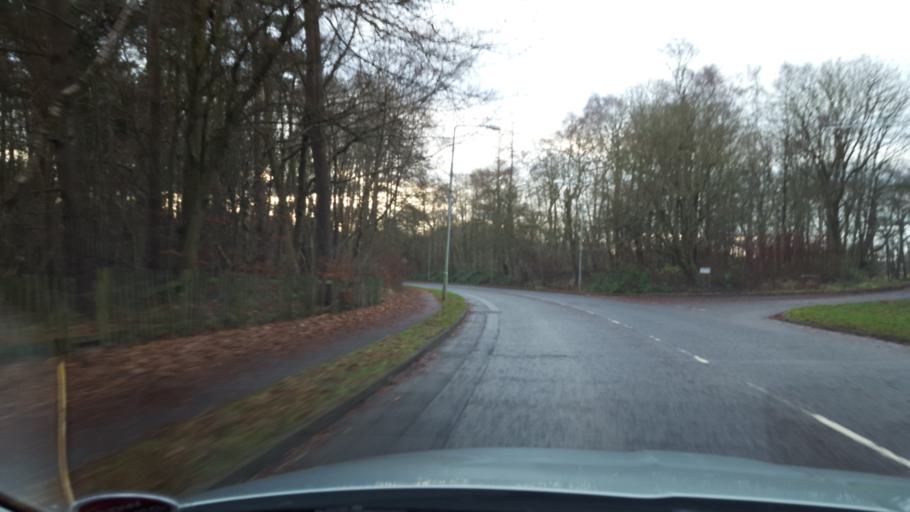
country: GB
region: Scotland
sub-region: West Lothian
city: Livingston
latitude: 55.8603
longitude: -3.5190
